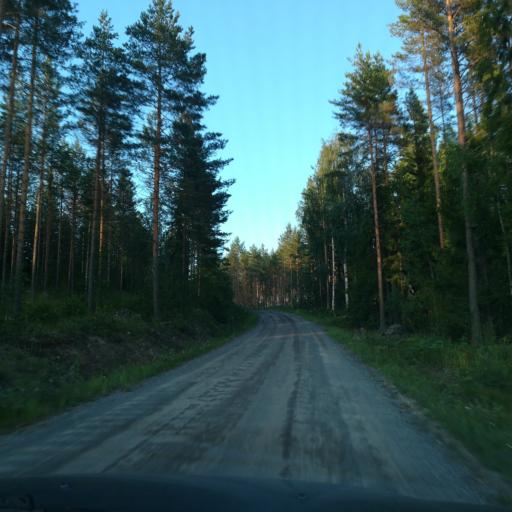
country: FI
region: Southern Savonia
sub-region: Mikkeli
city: Puumala
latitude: 61.4367
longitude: 28.4652
